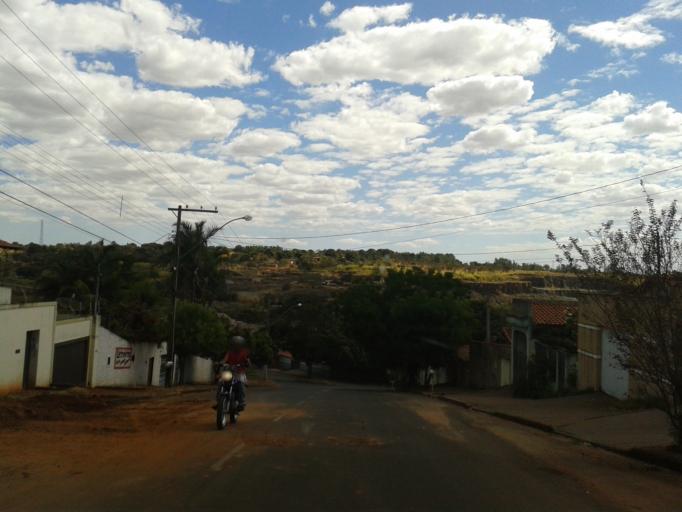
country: BR
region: Minas Gerais
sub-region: Ituiutaba
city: Ituiutaba
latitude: -18.9624
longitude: -49.4685
